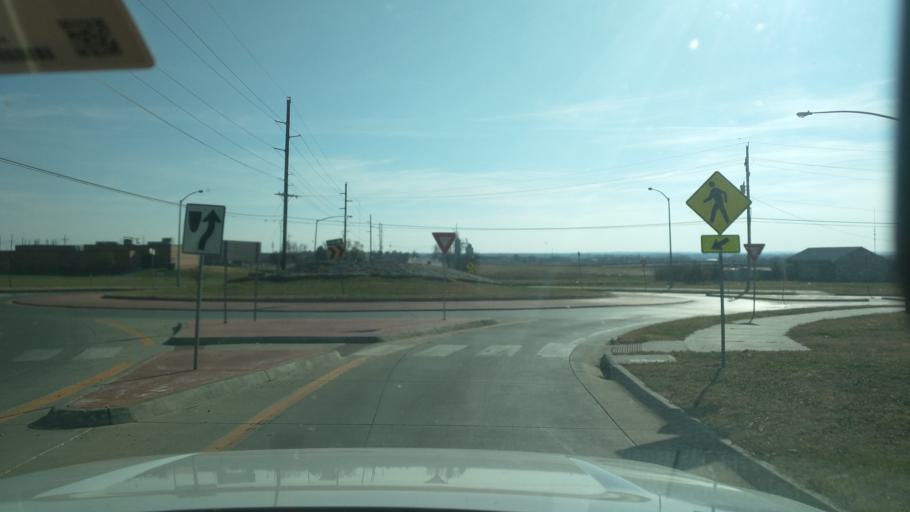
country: US
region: Kansas
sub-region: Lyon County
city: Emporia
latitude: 38.4201
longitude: -96.2262
